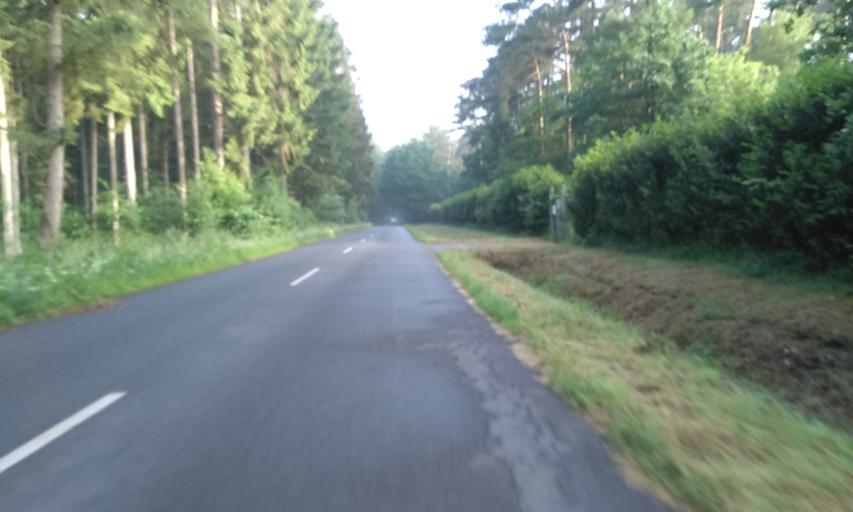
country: DE
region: Lower Saxony
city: Bargstedt
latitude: 53.4976
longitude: 9.4578
